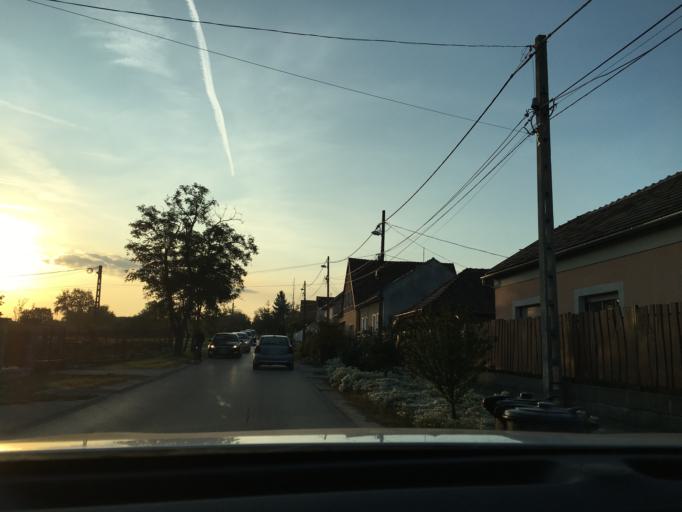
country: HU
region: Budapest
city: Budapest XVII. keruelet
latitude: 47.4757
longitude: 19.2594
